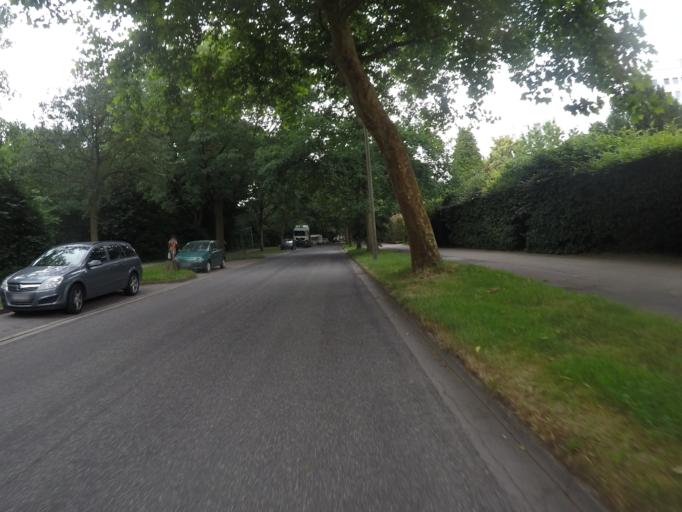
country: DE
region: Hamburg
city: Harburg
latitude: 53.4604
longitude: 9.9589
